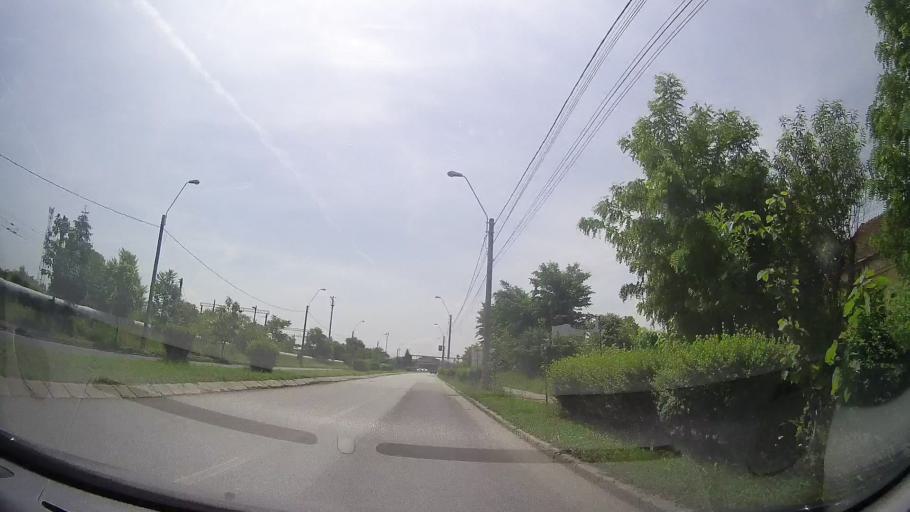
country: RO
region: Hunedoara
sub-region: Municipiul Deva
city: Deva
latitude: 45.8903
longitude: 22.9058
